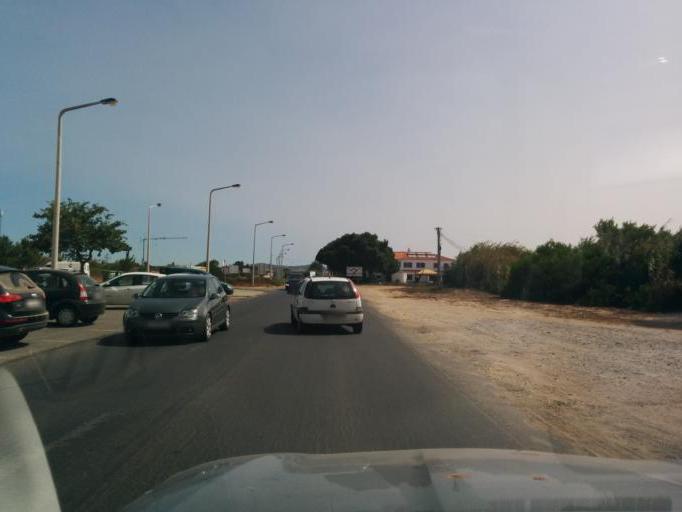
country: PT
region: Beja
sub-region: Odemira
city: Vila Nova de Milfontes
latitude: 37.7312
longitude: -8.7744
